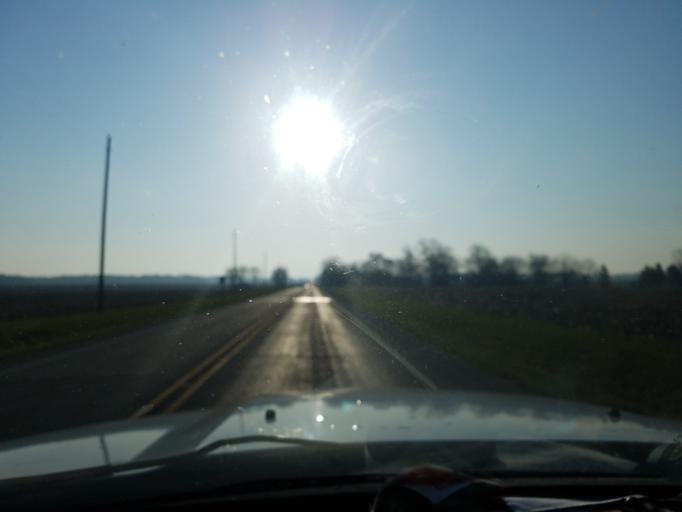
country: US
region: Indiana
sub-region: Vigo County
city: Seelyville
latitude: 39.3892
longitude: -87.2047
